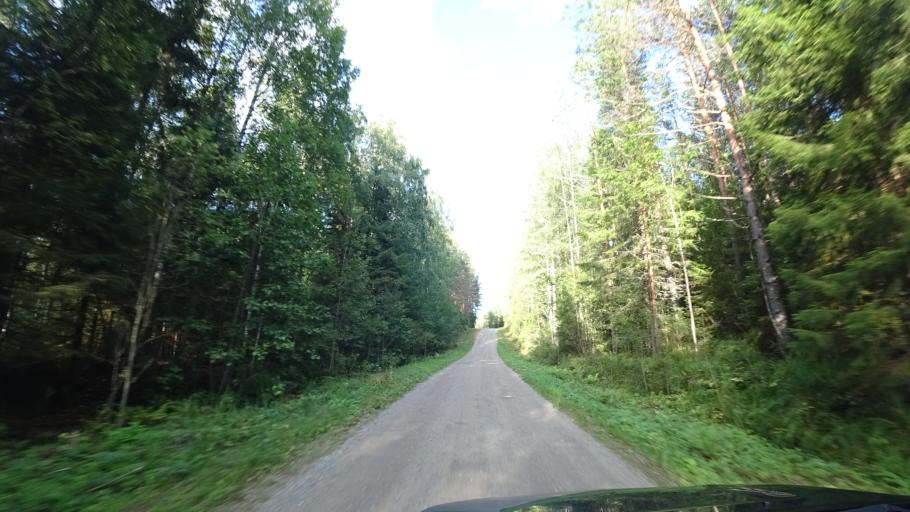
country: FI
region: Paijanne Tavastia
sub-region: Lahti
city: Auttoinen
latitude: 61.2213
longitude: 25.1833
